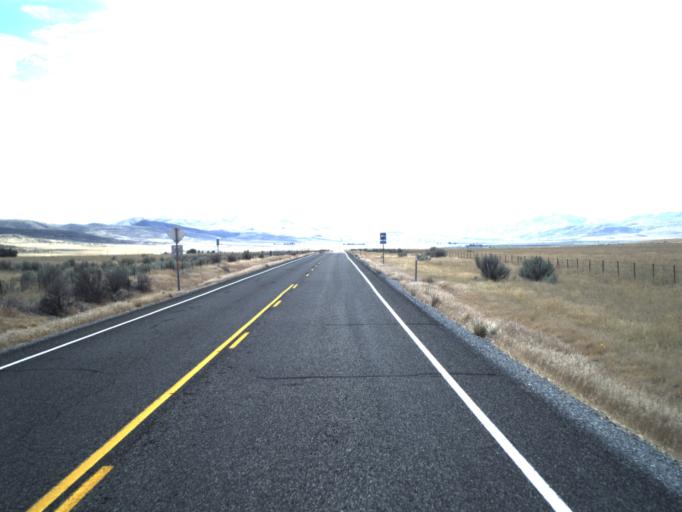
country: US
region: Utah
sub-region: Box Elder County
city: Garland
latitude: 41.8087
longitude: -112.4165
